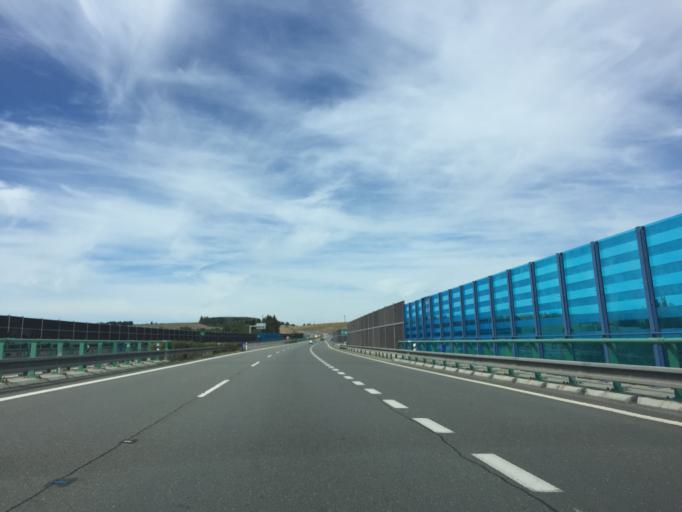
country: CZ
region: Jihocesky
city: Chotoviny
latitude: 49.5349
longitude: 14.6645
